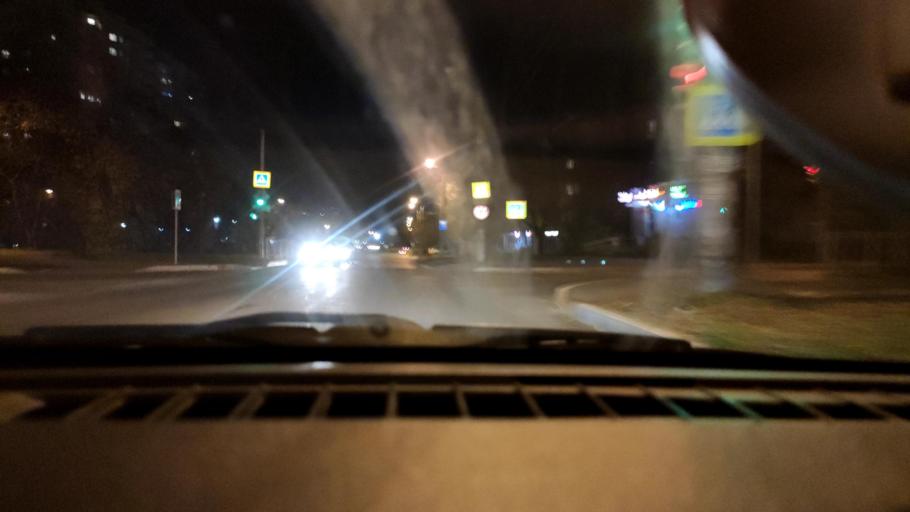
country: RU
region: Perm
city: Perm
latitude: 57.9862
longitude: 56.1947
